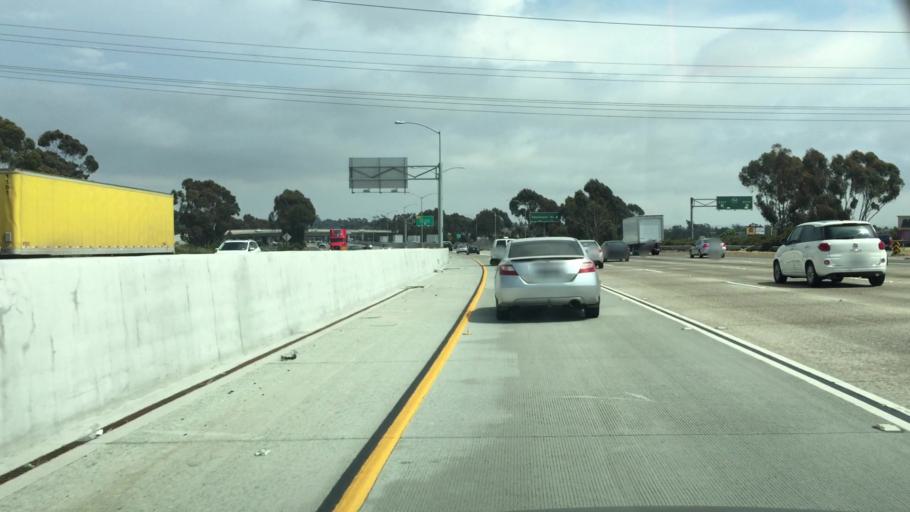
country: US
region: California
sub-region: San Diego County
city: Chula Vista
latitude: 32.6637
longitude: -117.0790
